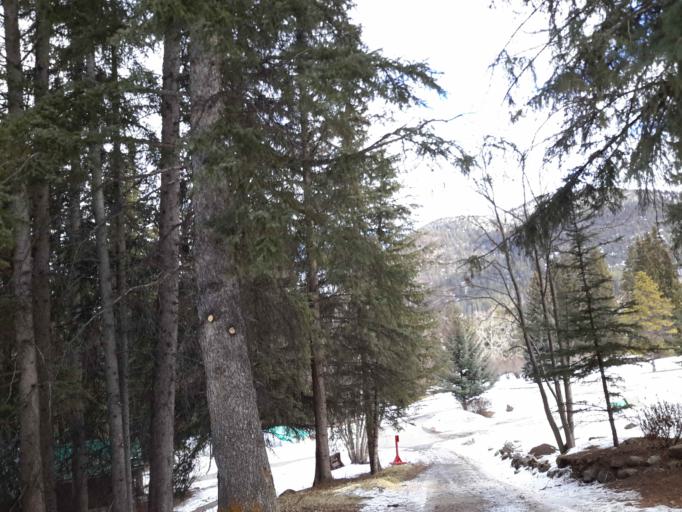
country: CA
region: Alberta
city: Banff
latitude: 51.1708
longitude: -115.5732
